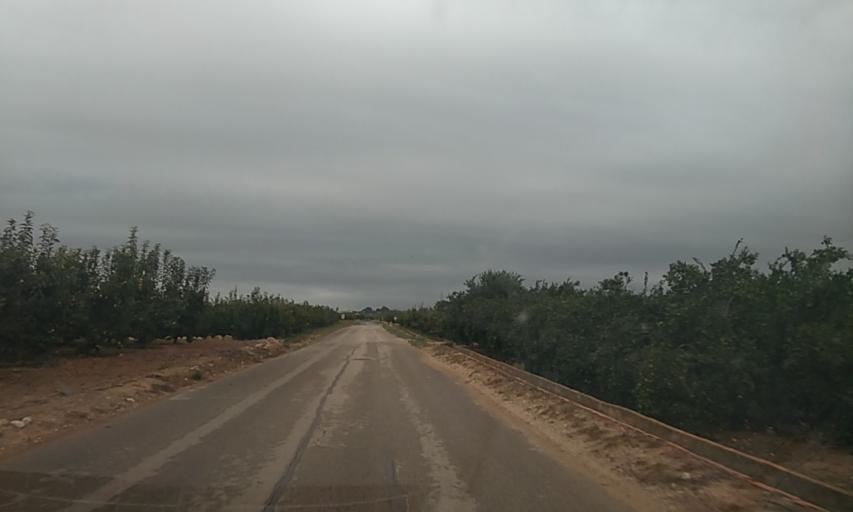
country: ES
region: Valencia
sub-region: Provincia de Valencia
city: Benimodo
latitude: 39.1886
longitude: -0.5356
